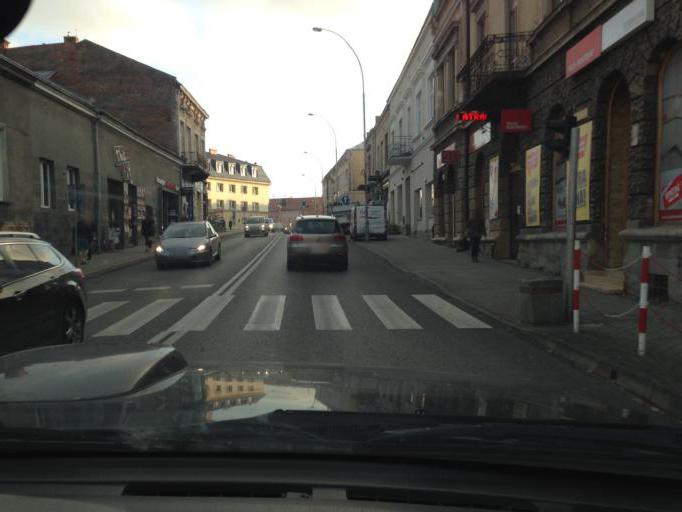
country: PL
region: Subcarpathian Voivodeship
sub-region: Powiat jasielski
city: Jaslo
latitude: 49.7488
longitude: 21.4733
